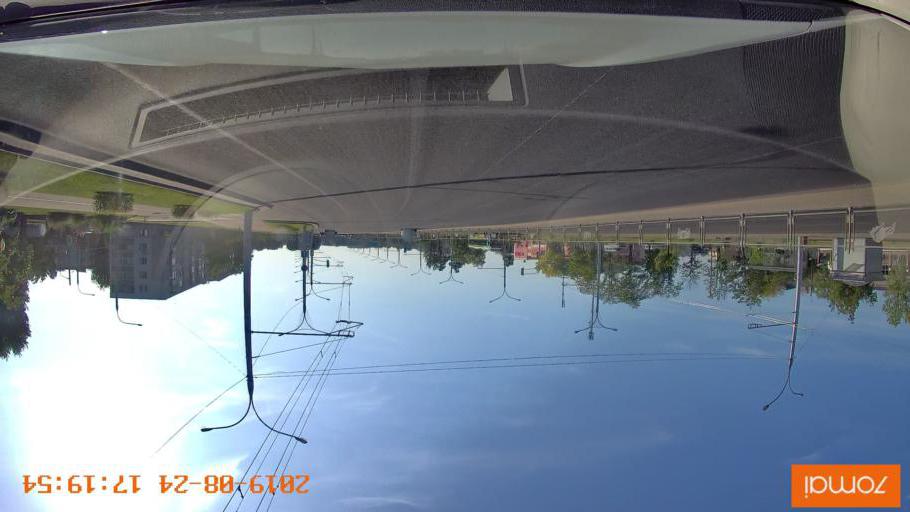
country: BY
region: Minsk
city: Vyaliki Trastsyanets
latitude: 53.8582
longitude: 27.6400
